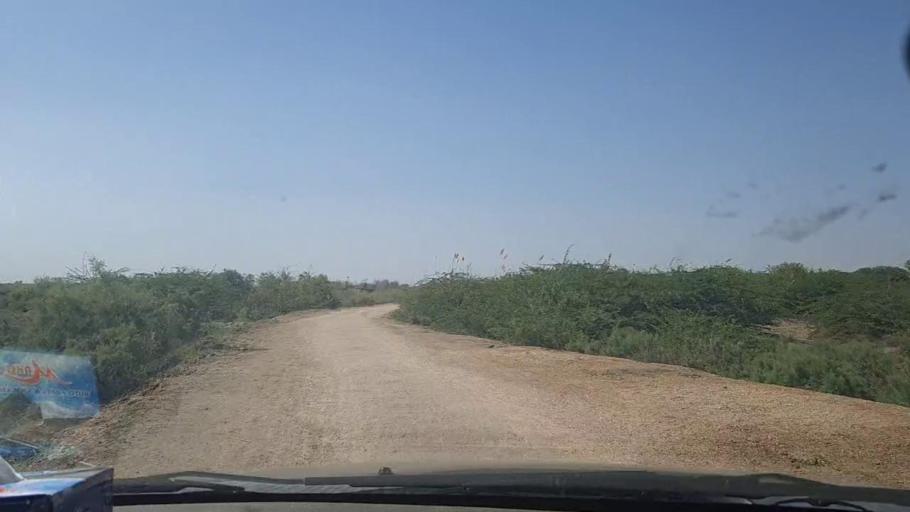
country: PK
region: Sindh
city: Chuhar Jamali
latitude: 24.2817
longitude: 67.7615
